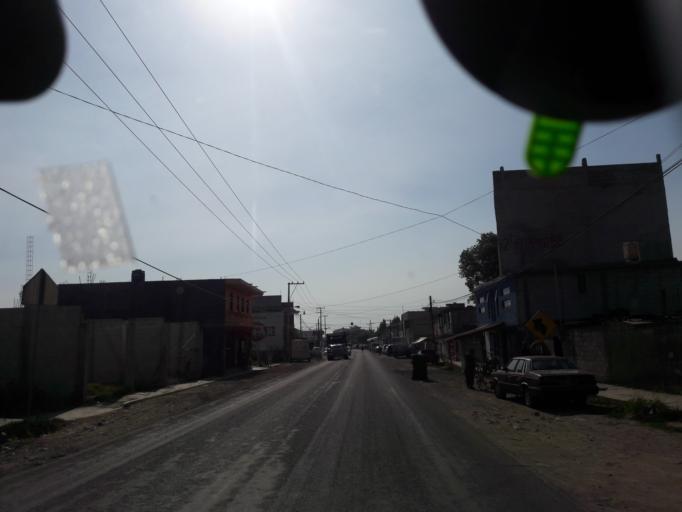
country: MX
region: Tlaxcala
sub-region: Ixtacuixtla de Mariano Matamoros
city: Villa Mariano Matamoros
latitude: 19.3086
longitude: -98.3770
